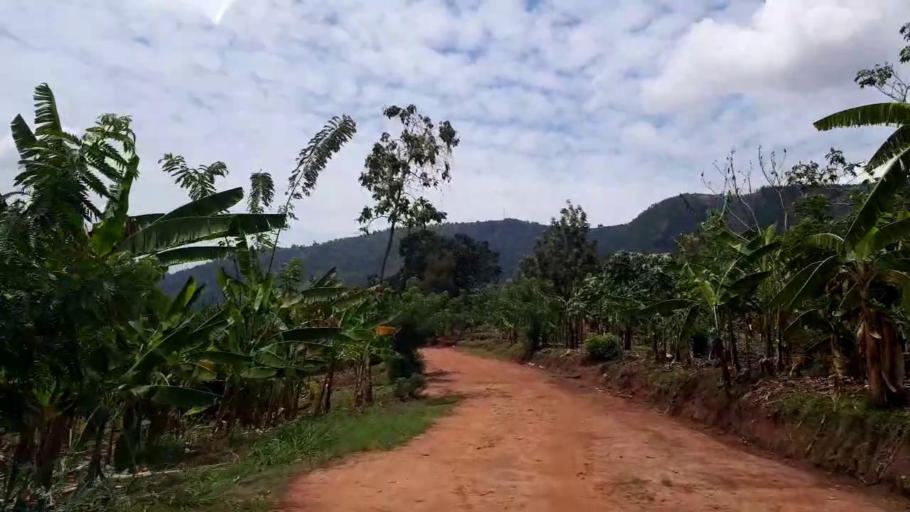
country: RW
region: Northern Province
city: Byumba
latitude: -1.4926
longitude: 30.1962
